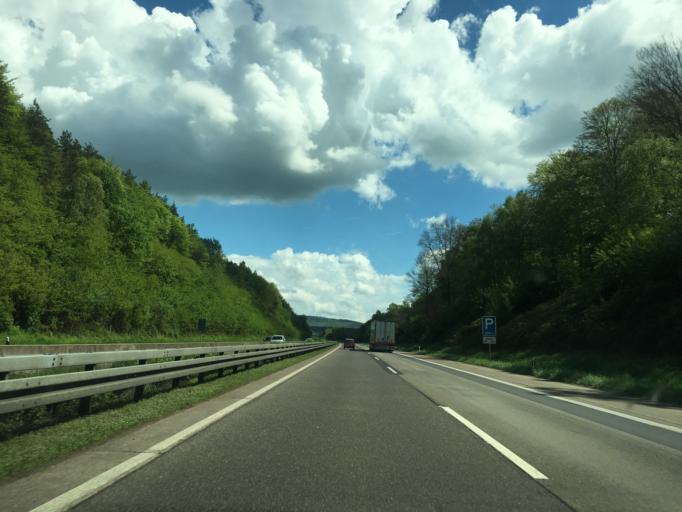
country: DE
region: Hesse
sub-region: Regierungsbezirk Kassel
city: Eichenzell
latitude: 50.4573
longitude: 9.7258
